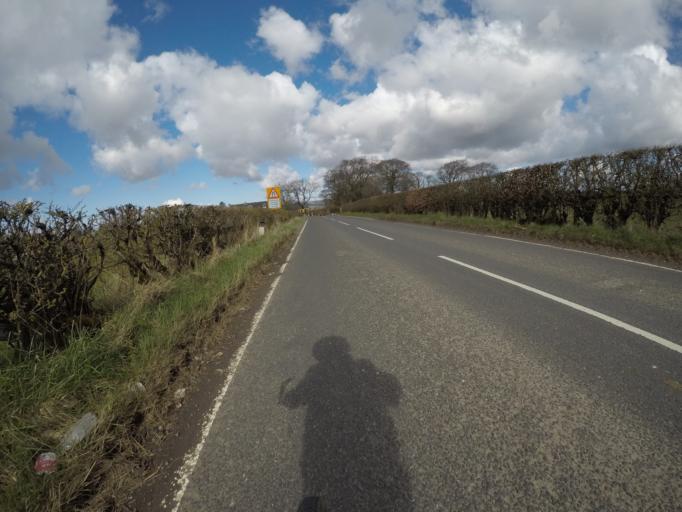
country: GB
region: Scotland
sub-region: North Ayrshire
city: Beith
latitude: 55.7371
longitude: -4.6196
